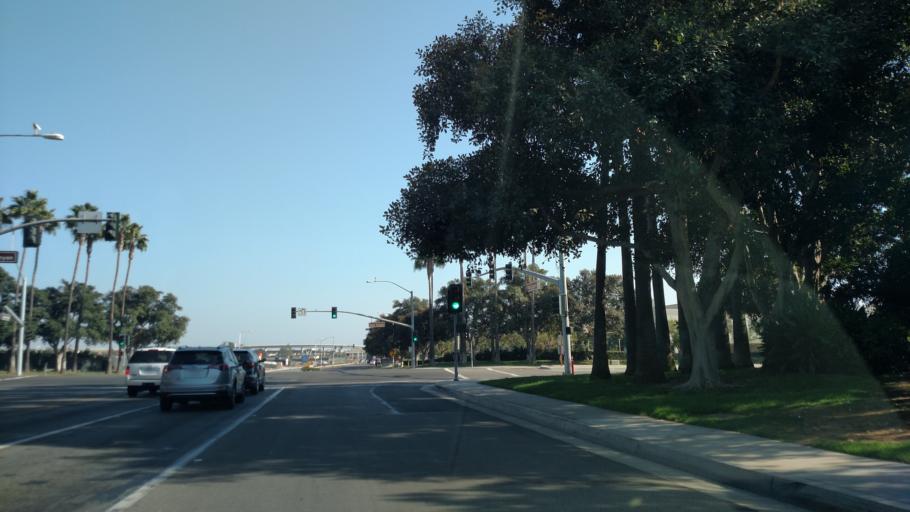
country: US
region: California
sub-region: Orange County
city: Irvine
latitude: 33.6737
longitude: -117.7630
